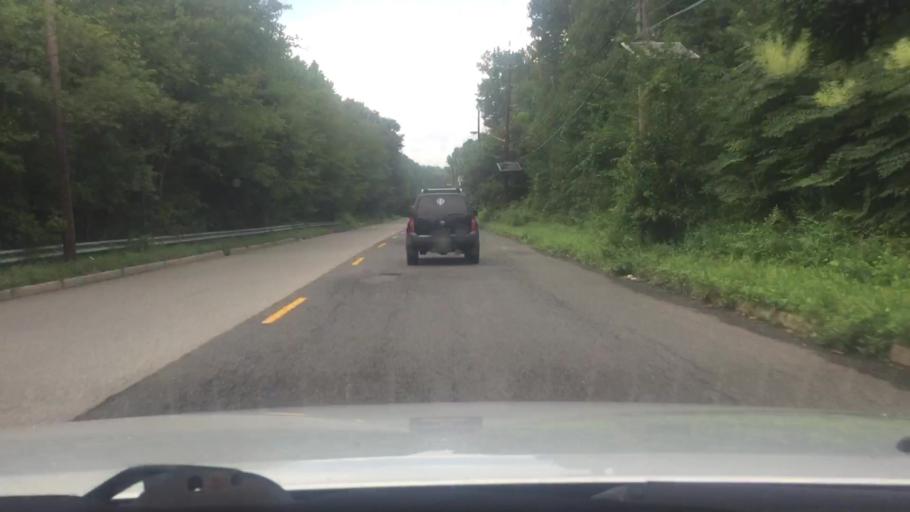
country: US
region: New Jersey
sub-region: Middlesex County
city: South River
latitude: 40.4515
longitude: -74.4091
